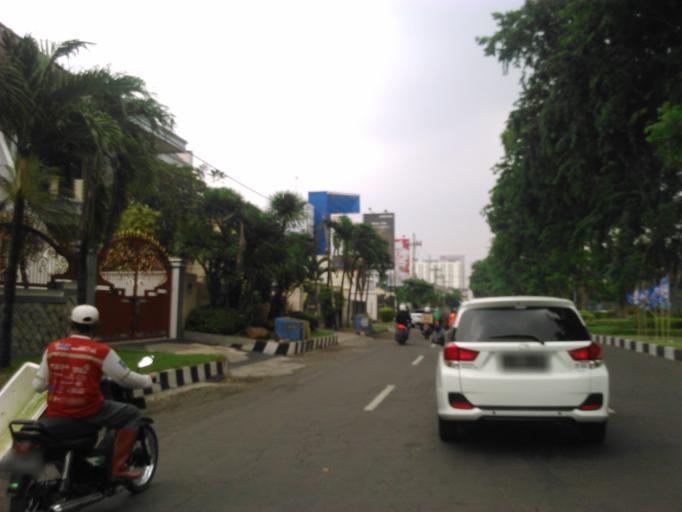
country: ID
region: East Java
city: Mulyorejo
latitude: -7.2807
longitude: 112.7760
